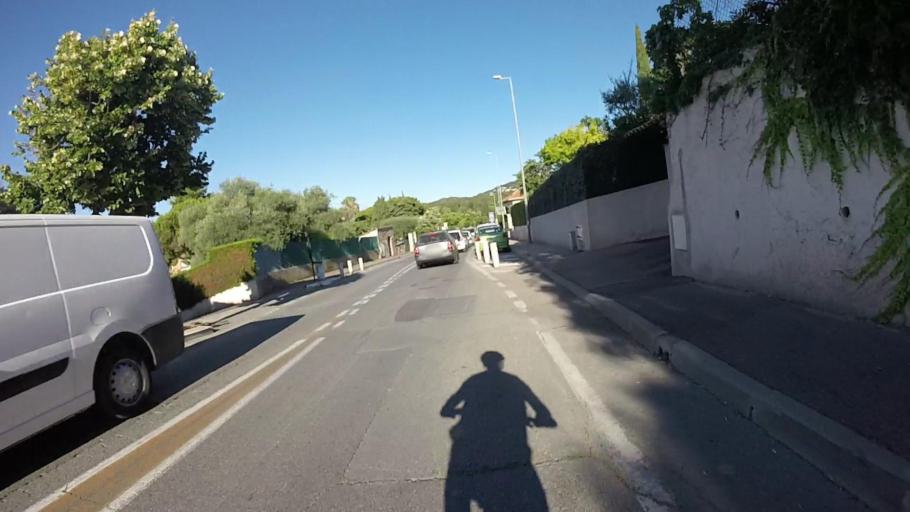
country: FR
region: Provence-Alpes-Cote d'Azur
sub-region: Departement des Alpes-Maritimes
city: Antibes
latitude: 43.5853
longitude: 7.0967
